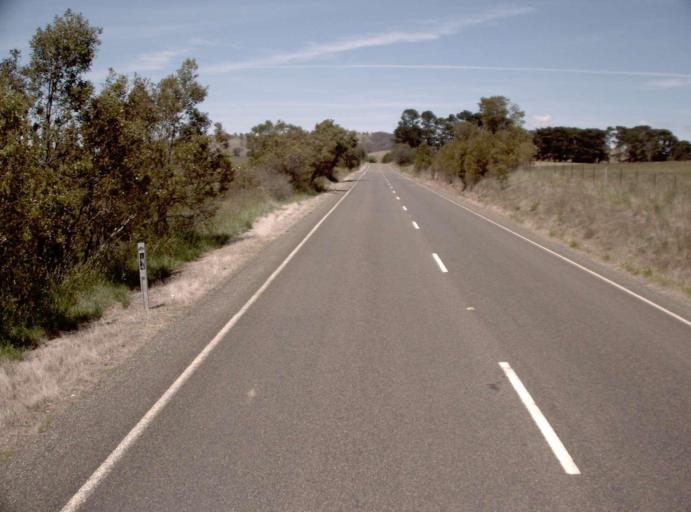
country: AU
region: Victoria
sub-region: Alpine
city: Mount Beauty
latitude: -37.1448
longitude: 147.6475
